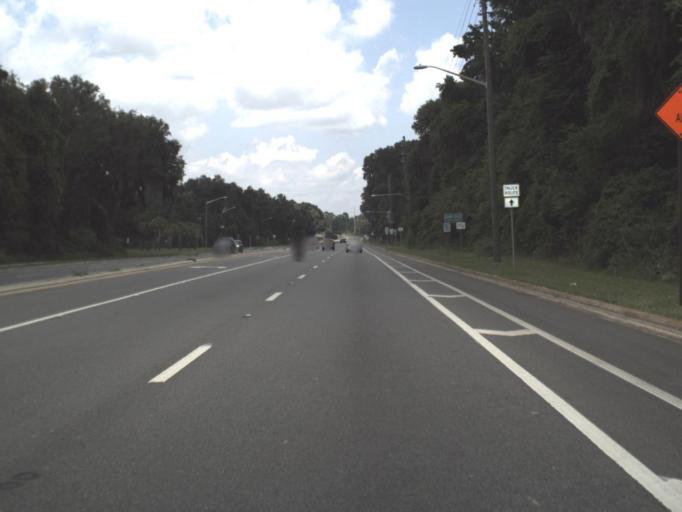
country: US
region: Florida
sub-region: Alachua County
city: Gainesville
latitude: 29.6168
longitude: -82.3348
